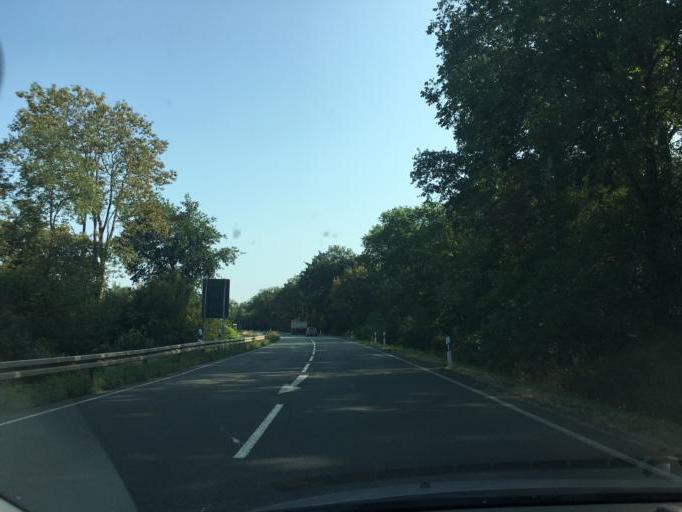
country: DE
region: Saxony-Anhalt
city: Plotzky
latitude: 52.0353
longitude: 11.7834
